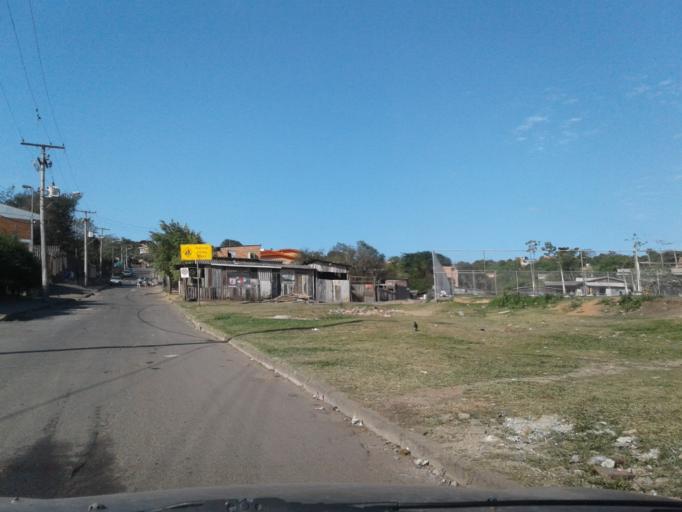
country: BR
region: Rio Grande do Sul
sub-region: Porto Alegre
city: Porto Alegre
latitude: -30.0492
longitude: -51.1567
